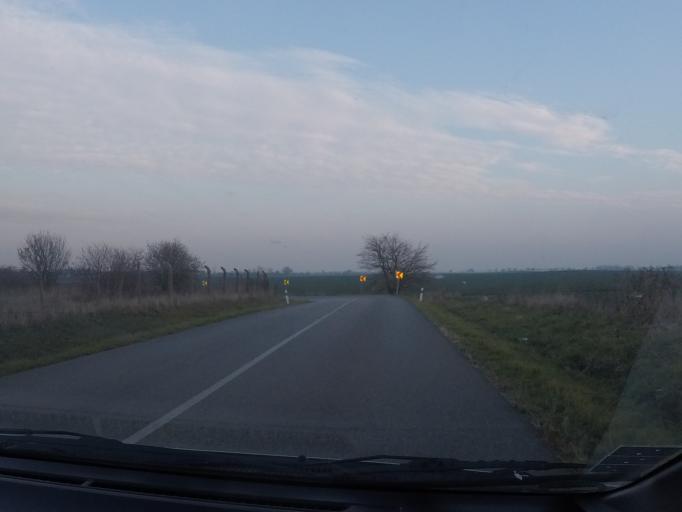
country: SK
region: Nitriansky
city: Zeliezovce
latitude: 48.0973
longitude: 18.5253
